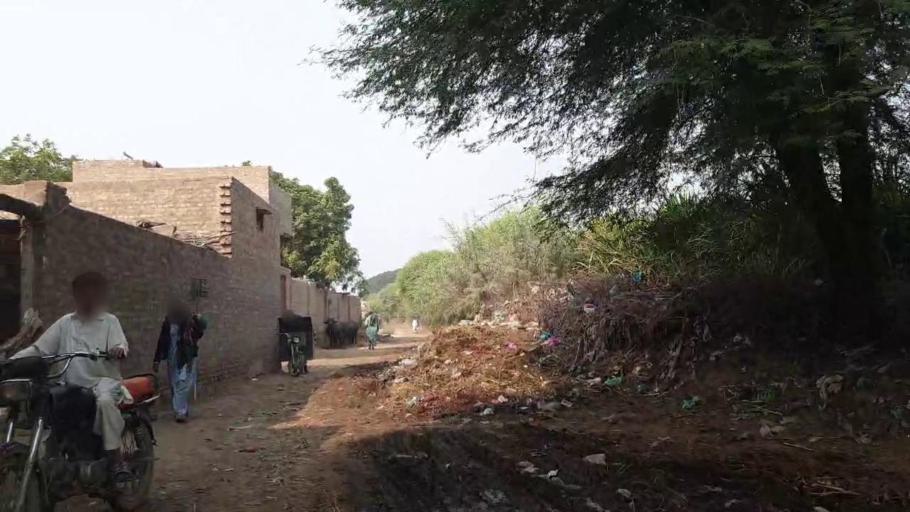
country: PK
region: Sindh
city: Tando Muhammad Khan
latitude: 25.1995
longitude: 68.5650
